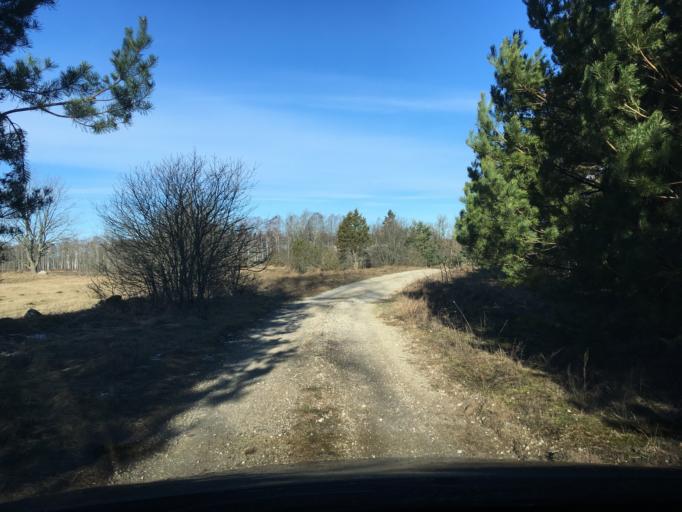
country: EE
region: Laeaene
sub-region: Lihula vald
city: Lihula
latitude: 58.5850
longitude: 23.7139
